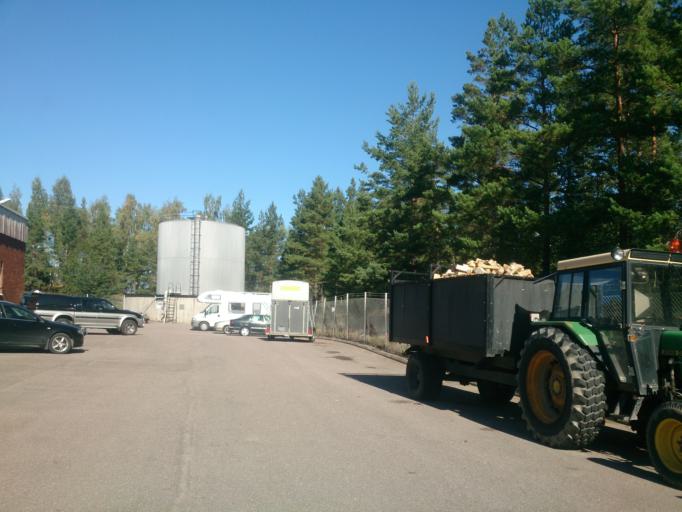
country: SE
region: OEstergoetland
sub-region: Atvidabergs Kommun
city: Atvidaberg
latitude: 58.2290
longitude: 15.9755
